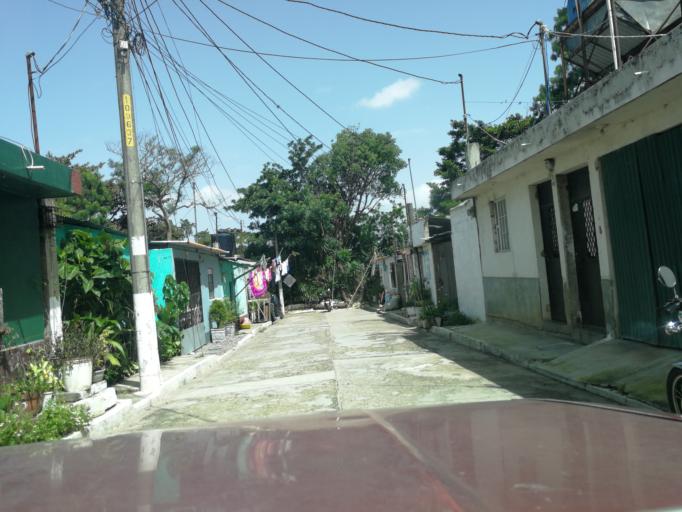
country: GT
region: Guatemala
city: Santa Catarina Pinula
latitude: 14.5481
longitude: -90.5187
